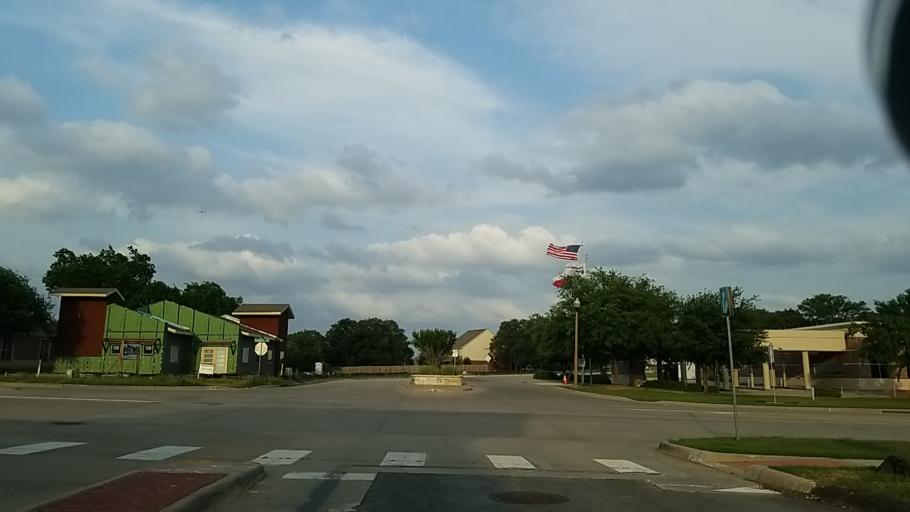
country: US
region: Texas
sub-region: Denton County
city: Denton
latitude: 33.1740
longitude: -97.1134
